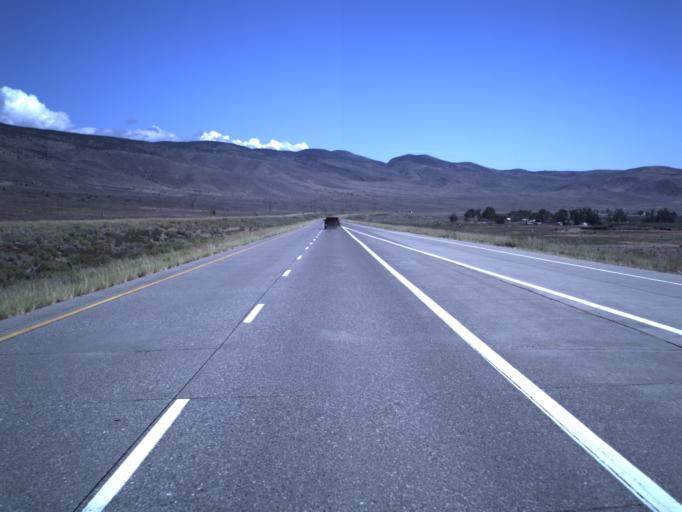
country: US
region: Utah
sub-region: Sevier County
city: Monroe
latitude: 38.6314
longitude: -112.2234
